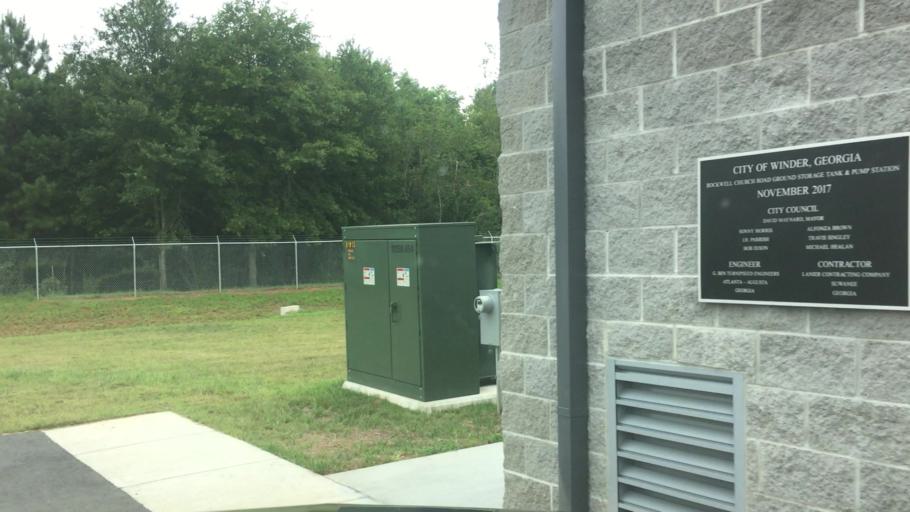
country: US
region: Georgia
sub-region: Barrow County
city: Winder
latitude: 34.0220
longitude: -83.7613
